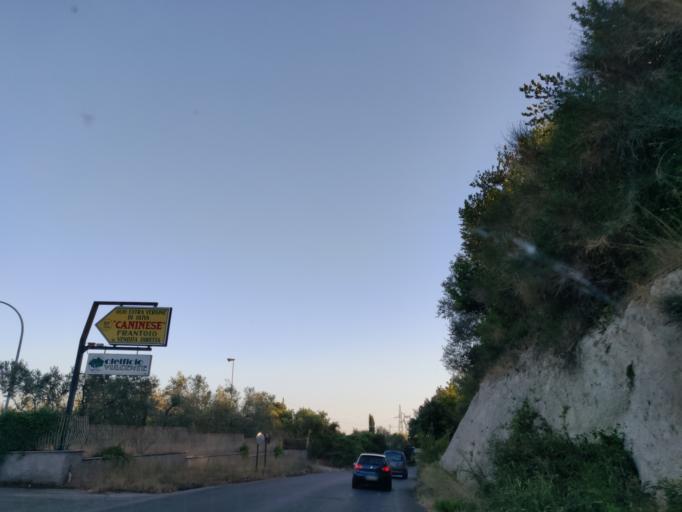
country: IT
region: Latium
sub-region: Provincia di Viterbo
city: Canino
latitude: 42.4567
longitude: 11.7412
